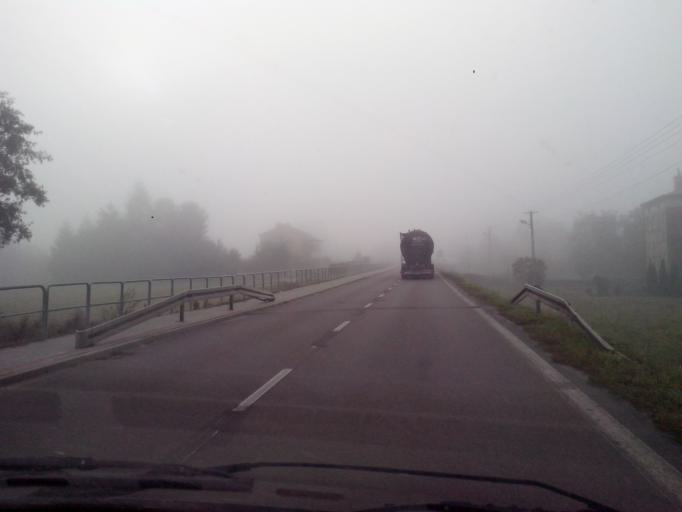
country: PL
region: Subcarpathian Voivodeship
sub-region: Przemysl
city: Przemysl
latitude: 49.7983
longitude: 22.7151
